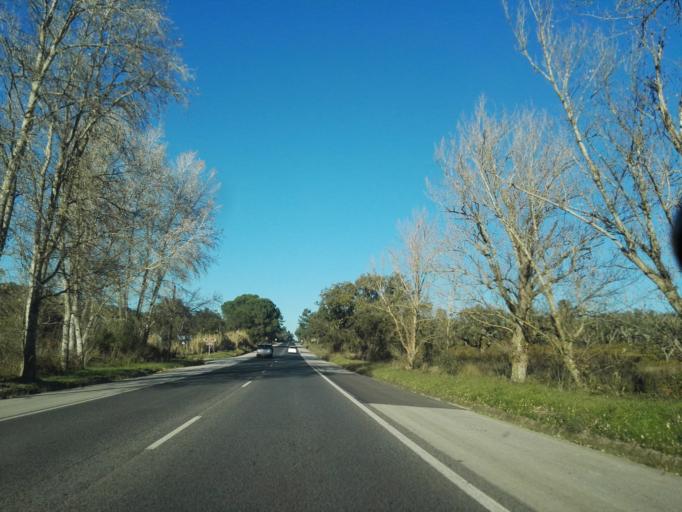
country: PT
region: Lisbon
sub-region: Azambuja
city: Azambuja
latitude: 39.0836
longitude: -8.8568
